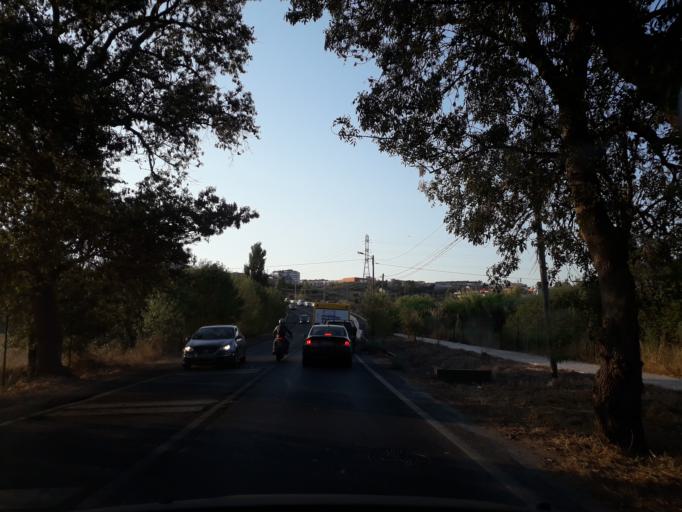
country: PT
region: Lisbon
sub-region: Odivelas
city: Pontinha
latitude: 38.7740
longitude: -9.2046
